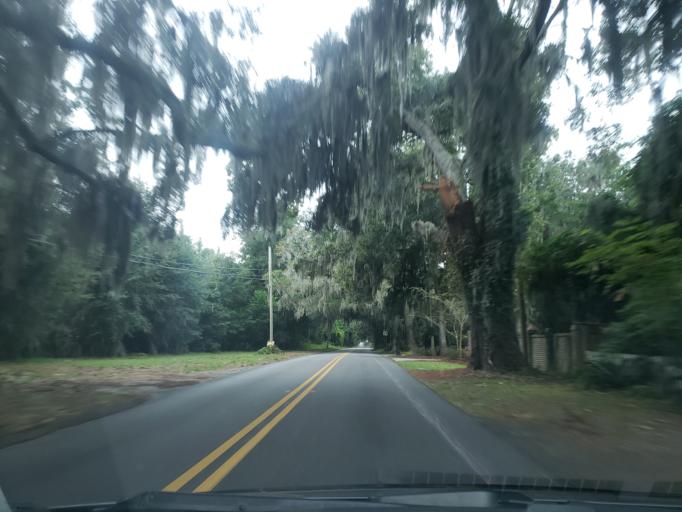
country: US
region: Georgia
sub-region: Chatham County
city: Montgomery
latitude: 31.9618
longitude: -81.1016
